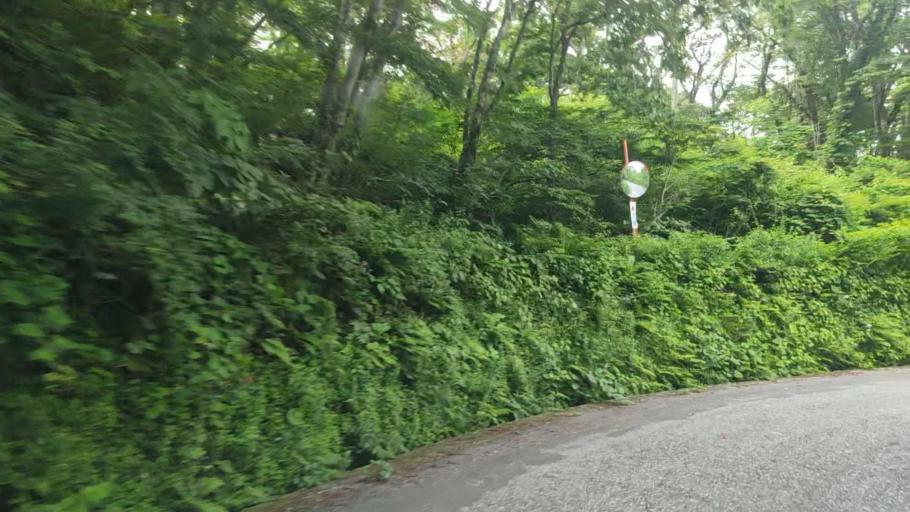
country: JP
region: Tottori
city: Yonago
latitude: 35.3620
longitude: 133.5247
